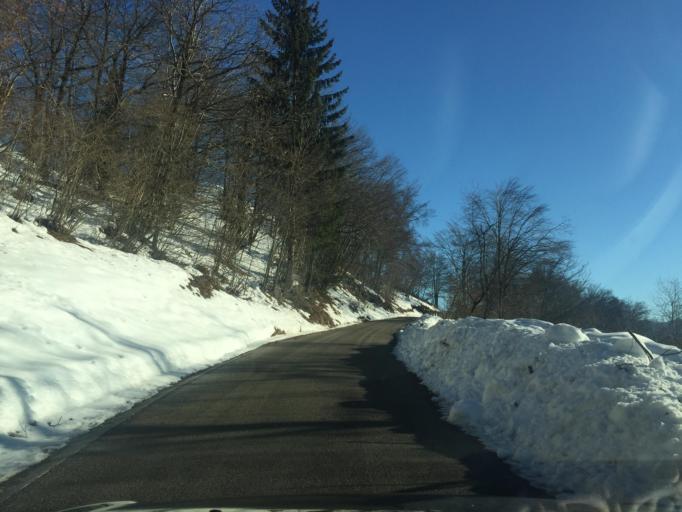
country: IT
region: Friuli Venezia Giulia
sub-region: Provincia di Udine
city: Lauco
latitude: 46.4327
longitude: 12.9699
